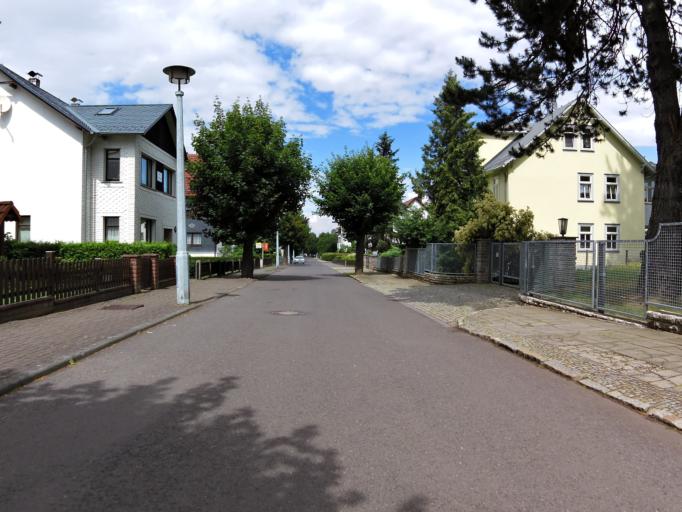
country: DE
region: Thuringia
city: Tabarz
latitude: 50.8723
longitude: 10.5123
